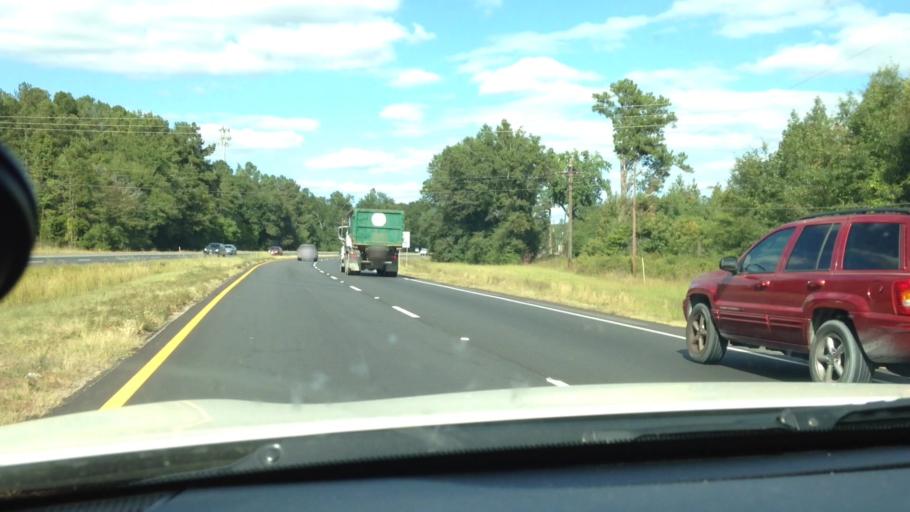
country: US
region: Georgia
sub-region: Richmond County
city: Hephzibah
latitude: 33.4155
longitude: -82.0854
